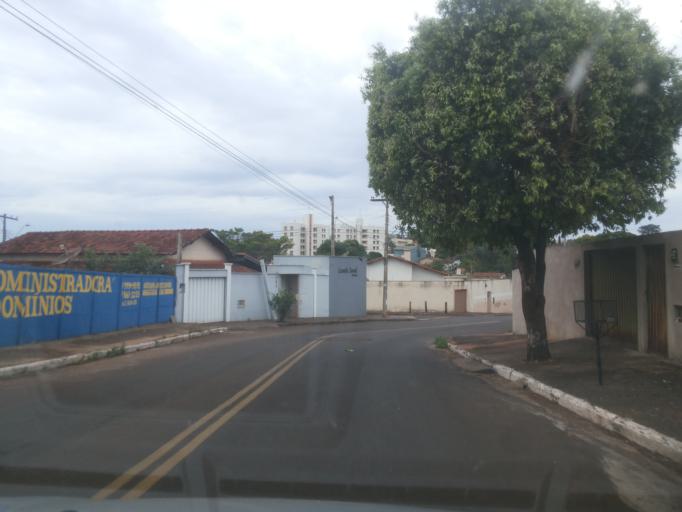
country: BR
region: Minas Gerais
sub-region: Ituiutaba
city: Ituiutaba
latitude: -18.9684
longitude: -49.4708
